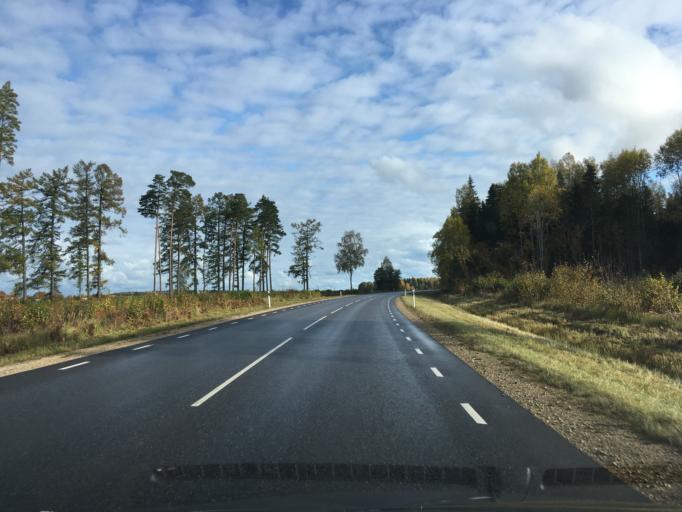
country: EE
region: Harju
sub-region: Raasiku vald
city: Raasiku
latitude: 59.2083
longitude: 25.1883
